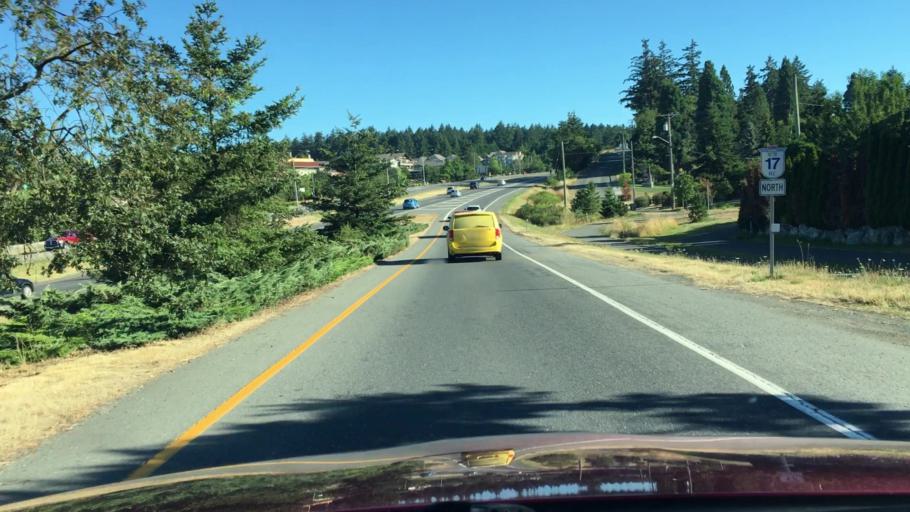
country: CA
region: British Columbia
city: Victoria
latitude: 48.4995
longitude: -123.3846
